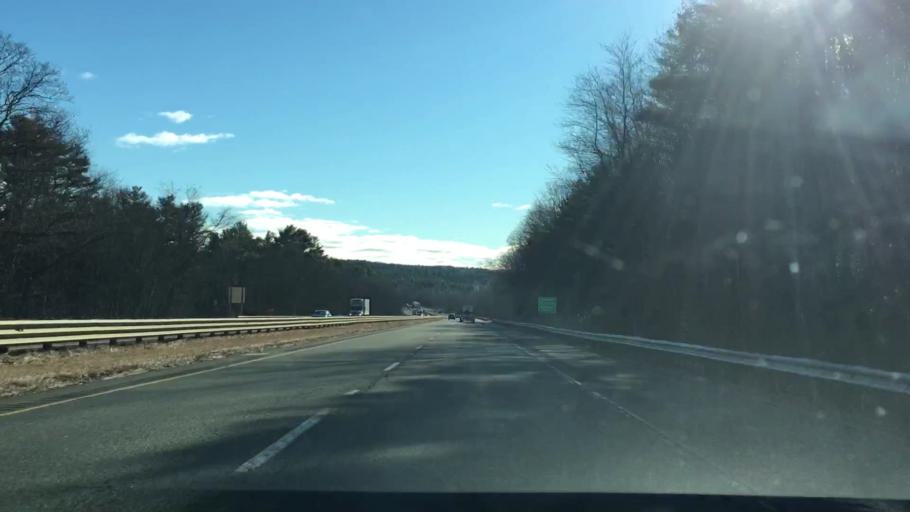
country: US
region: Massachusetts
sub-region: Worcester County
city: Fiskdale
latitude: 42.1412
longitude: -72.1363
